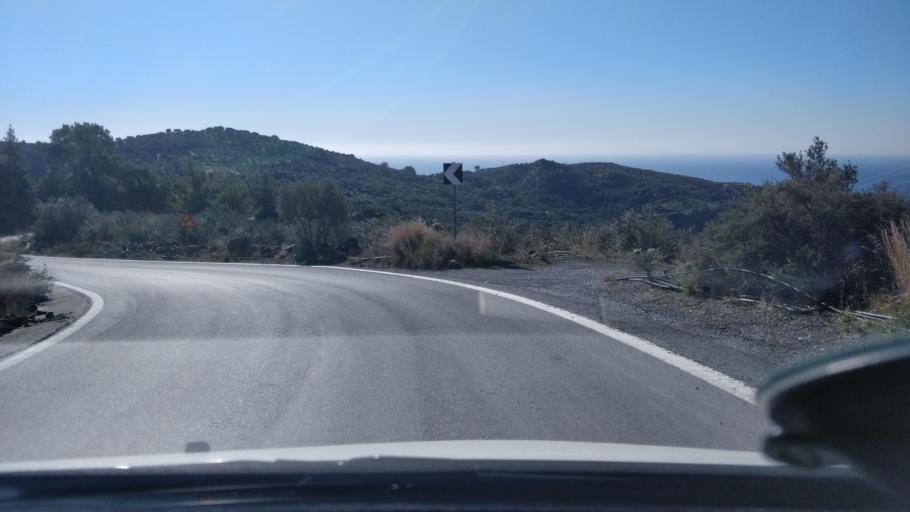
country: GR
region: Crete
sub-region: Nomos Irakleiou
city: Kastelli
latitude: 35.0224
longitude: 25.4480
